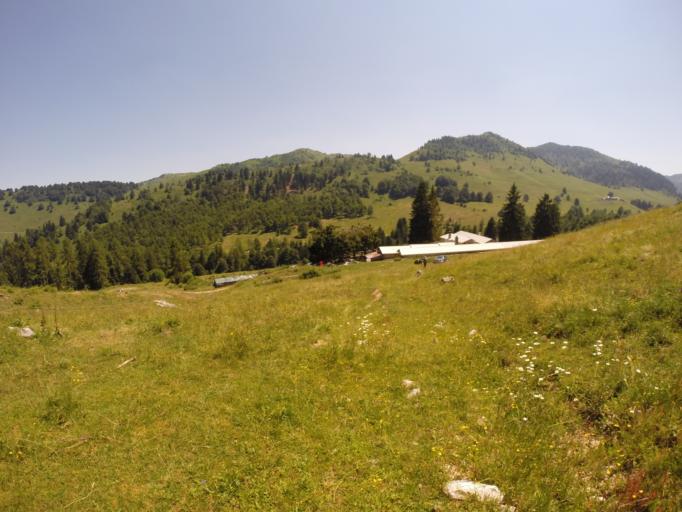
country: IT
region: Veneto
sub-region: Provincia di Treviso
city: Crespano del Grappa
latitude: 45.9012
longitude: 11.8298
